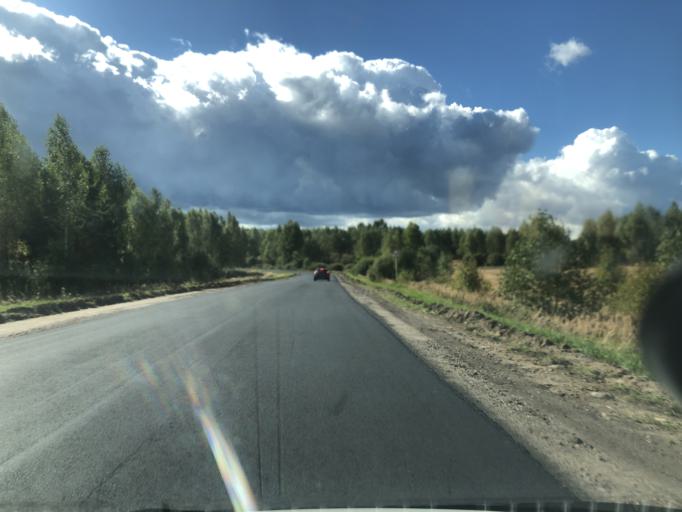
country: RU
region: Jaroslavl
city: Petrovsk
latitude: 56.9659
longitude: 39.3833
